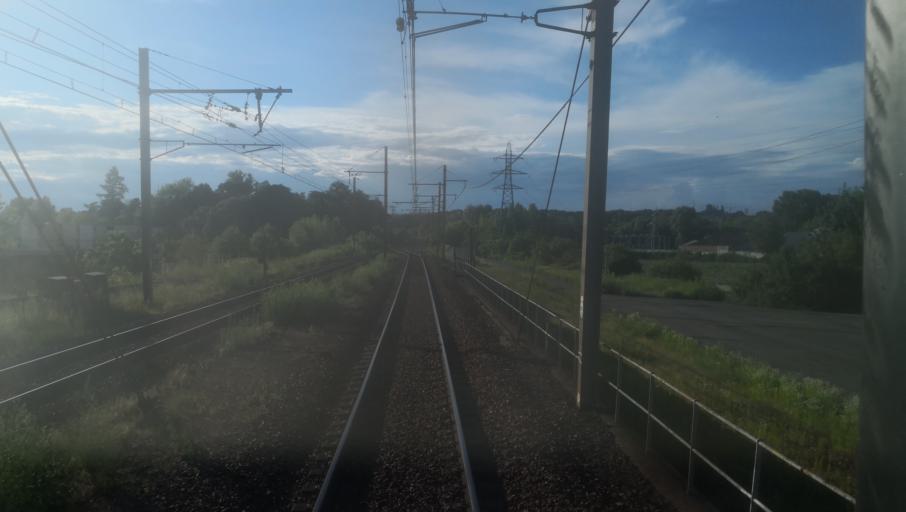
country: FR
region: Centre
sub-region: Departement du Cher
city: Vierzon
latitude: 47.2128
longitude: 2.0971
